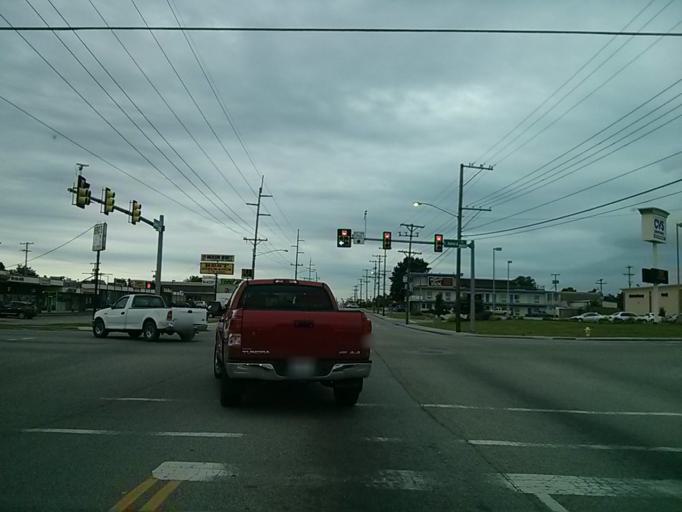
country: US
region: Oklahoma
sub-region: Tulsa County
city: Tulsa
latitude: 36.1610
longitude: -95.9046
